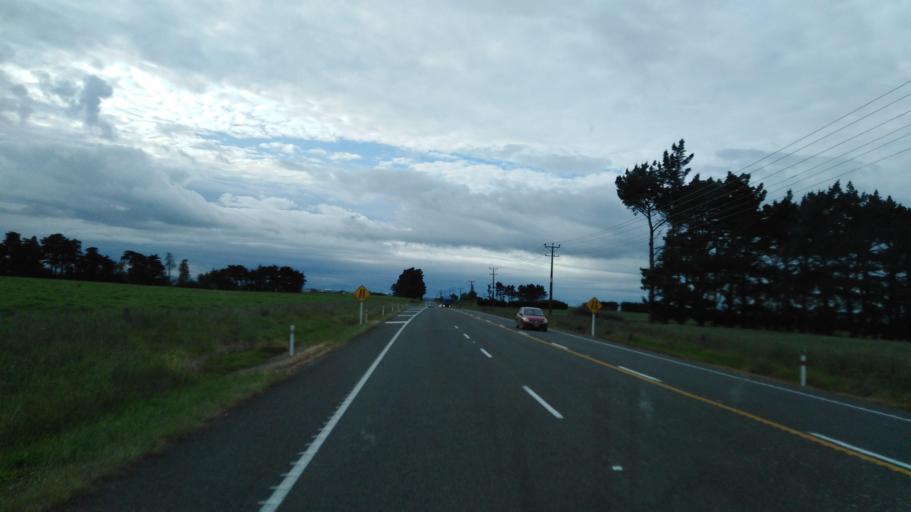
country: NZ
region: Manawatu-Wanganui
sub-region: Rangitikei District
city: Bulls
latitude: -40.1355
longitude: 175.3638
